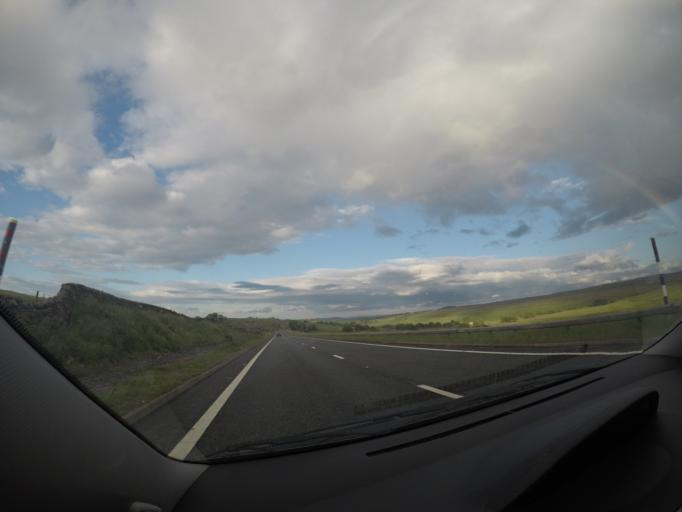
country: GB
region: England
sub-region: County Durham
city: Bowes
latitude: 54.5117
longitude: -2.0654
